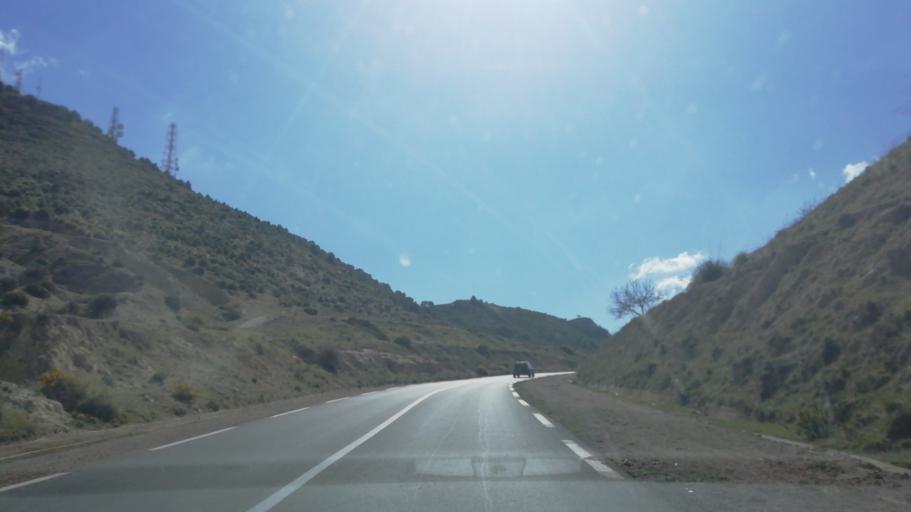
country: DZ
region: Mascara
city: Mascara
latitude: 35.4773
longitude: 0.1588
